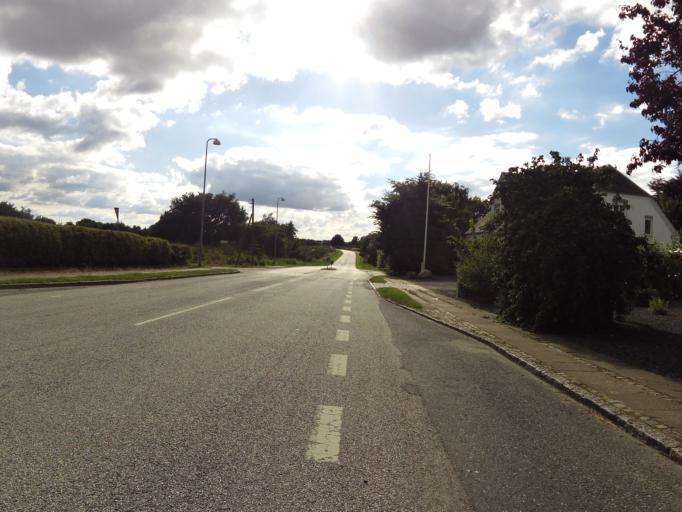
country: DK
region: South Denmark
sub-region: Haderslev Kommune
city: Haderslev
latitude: 55.2079
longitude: 9.4388
